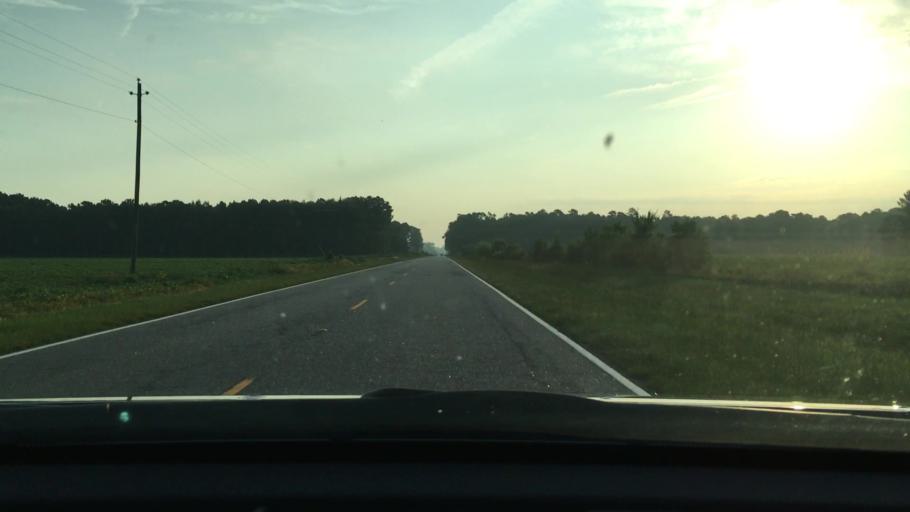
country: US
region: South Carolina
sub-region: Lee County
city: Bishopville
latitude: 34.0845
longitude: -80.1918
